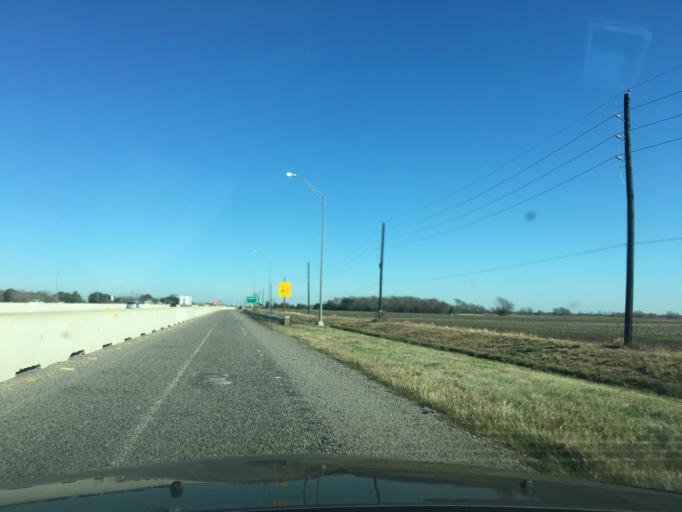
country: US
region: Texas
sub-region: Fort Bend County
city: Pleak
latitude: 29.4885
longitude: -95.9254
